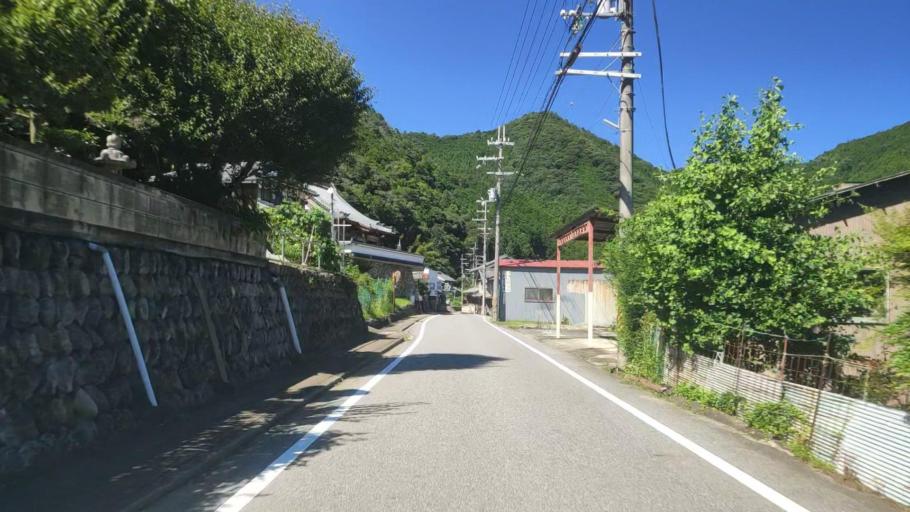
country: JP
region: Nara
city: Yoshino-cho
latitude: 34.3901
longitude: 135.9210
